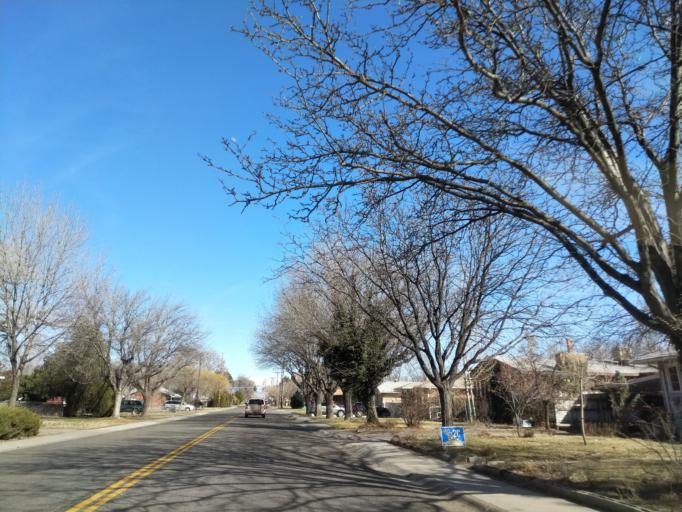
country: US
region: Colorado
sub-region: Mesa County
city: Grand Junction
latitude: 39.0846
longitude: -108.5635
